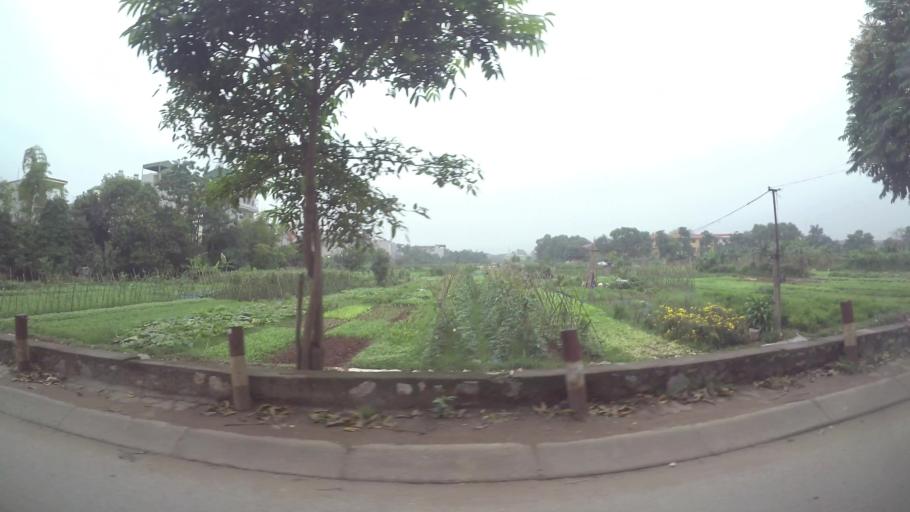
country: VN
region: Ha Noi
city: Hai BaTrung
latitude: 20.9846
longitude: 105.8894
